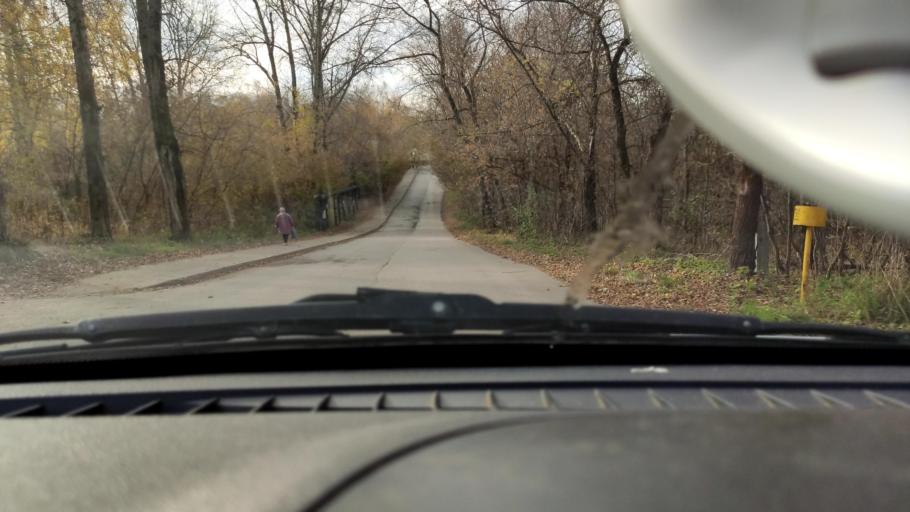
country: RU
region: Perm
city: Polazna
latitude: 58.1244
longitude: 56.3830
